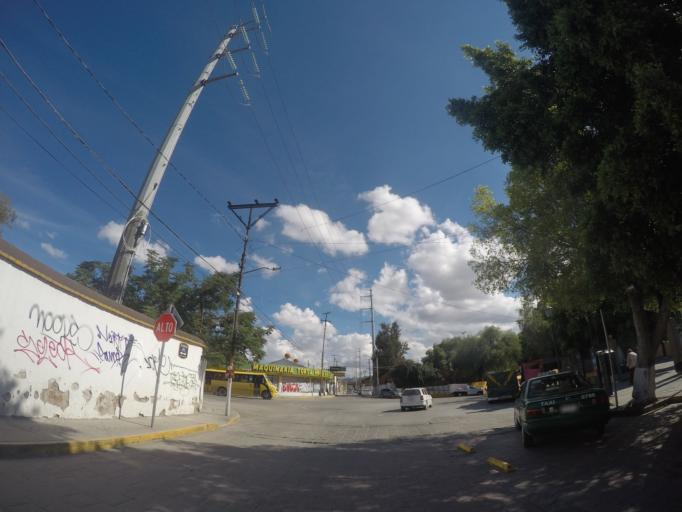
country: MX
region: San Luis Potosi
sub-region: San Luis Potosi
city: San Luis Potosi
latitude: 22.1541
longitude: -100.9678
